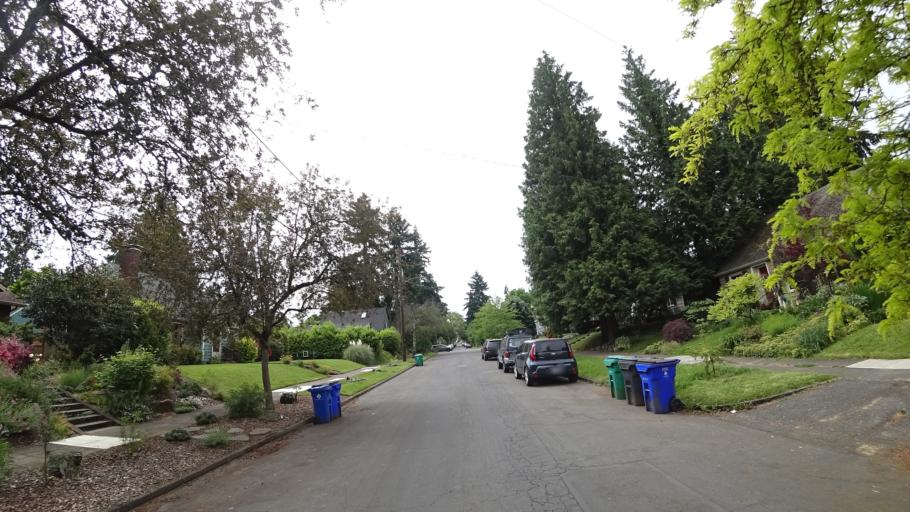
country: US
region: Oregon
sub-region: Multnomah County
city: Portland
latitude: 45.5672
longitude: -122.6339
